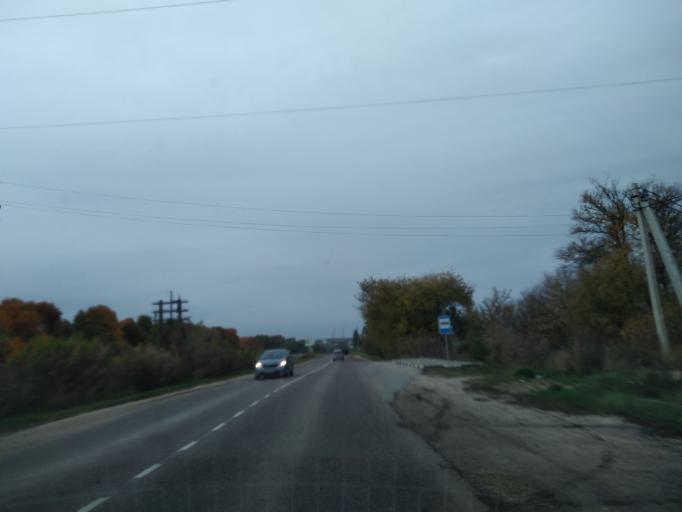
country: RU
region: Lipetsk
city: Zadonsk
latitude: 52.3937
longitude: 38.8995
